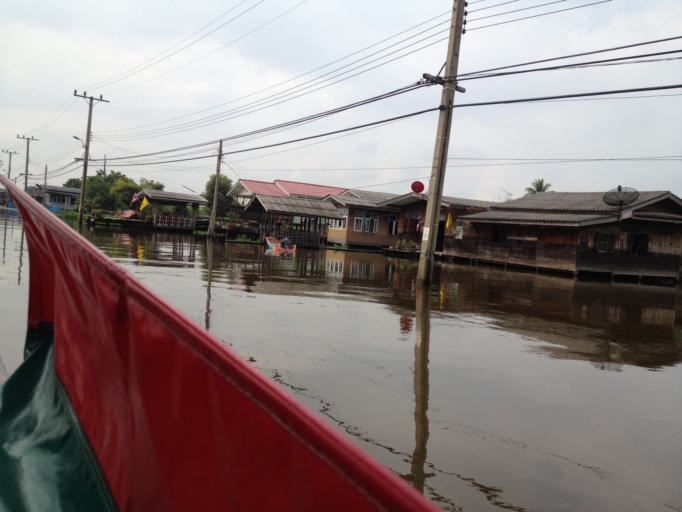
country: TH
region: Nonthaburi
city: Bang Kruai
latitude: 13.7981
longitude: 100.4710
